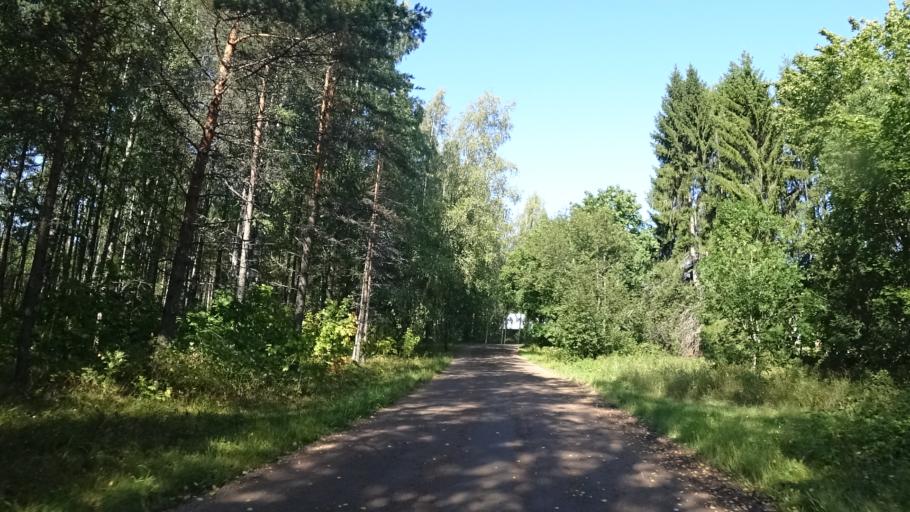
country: FI
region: Kymenlaakso
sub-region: Kotka-Hamina
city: Hamina
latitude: 60.5399
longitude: 27.2210
